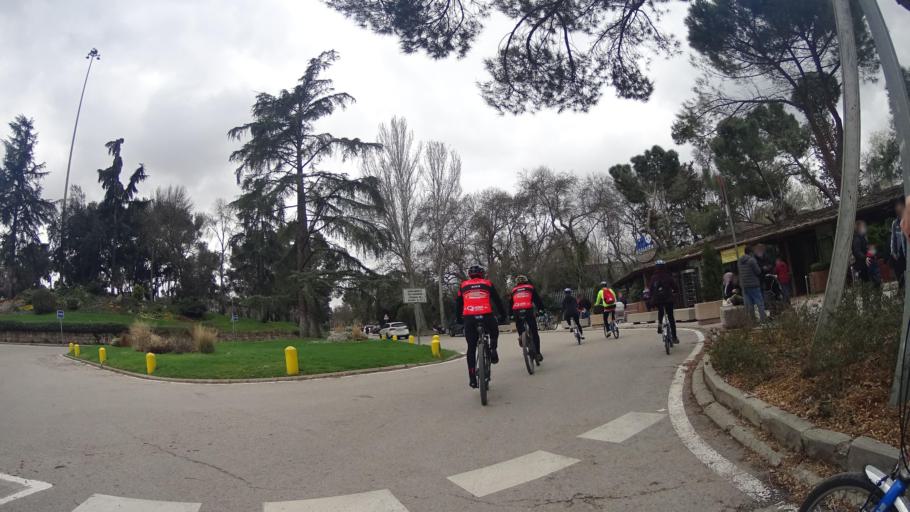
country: ES
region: Madrid
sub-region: Provincia de Madrid
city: Latina
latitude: 40.4090
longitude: -3.7609
